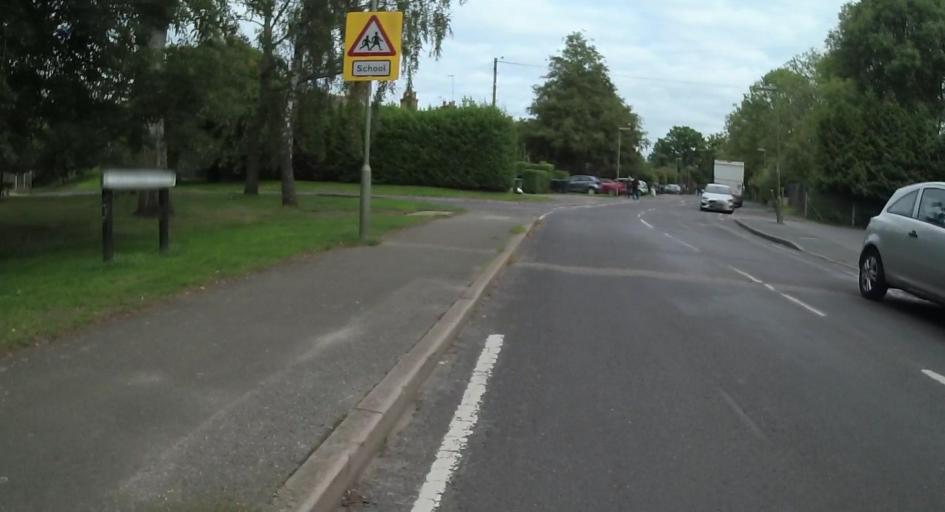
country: GB
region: England
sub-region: Surrey
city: Knaphill
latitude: 51.3163
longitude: -0.6077
